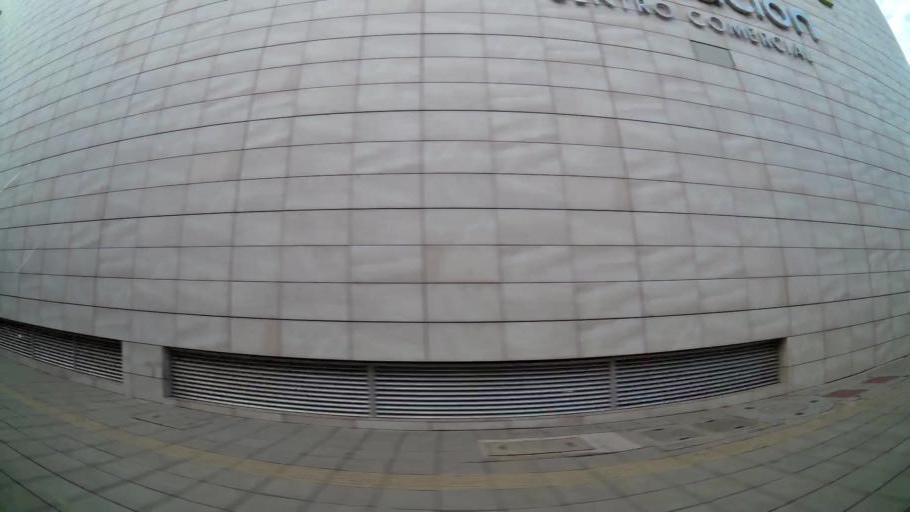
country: CO
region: Valle del Cauca
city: Cali
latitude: 3.4643
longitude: -76.5124
